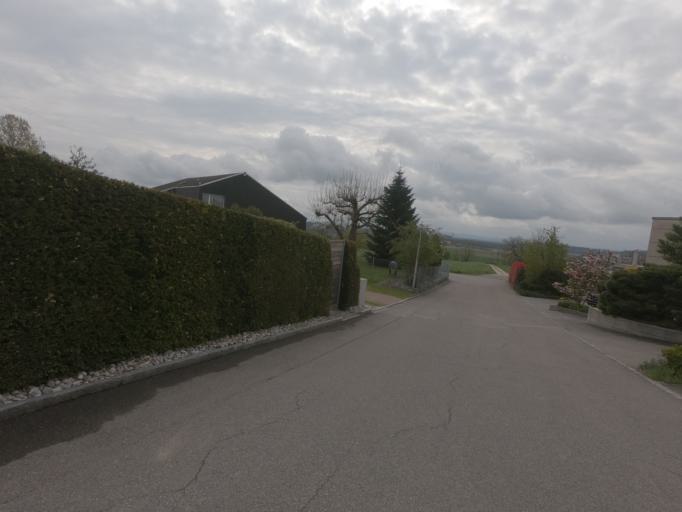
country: CH
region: Solothurn
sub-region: Bezirk Lebern
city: Riedholz
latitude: 47.2191
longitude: 7.5584
